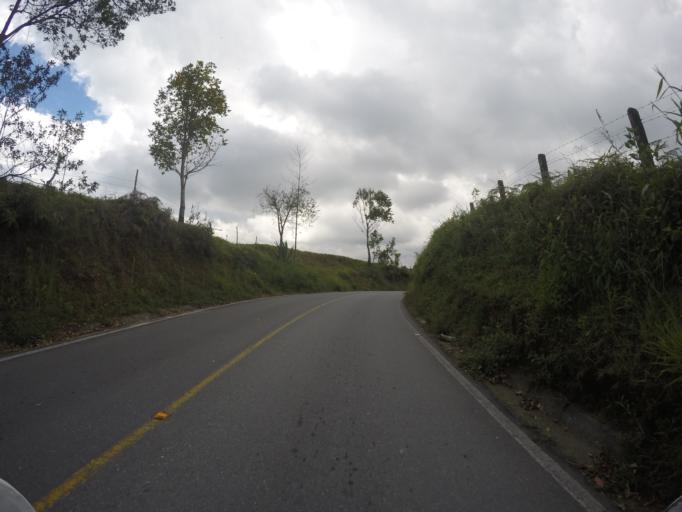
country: CO
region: Quindio
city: Filandia
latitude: 4.6602
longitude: -75.6739
